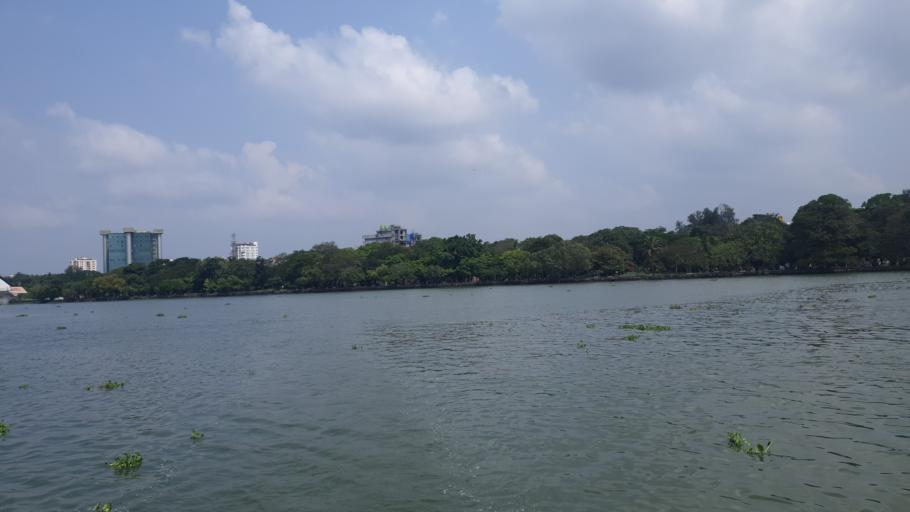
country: IN
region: Kerala
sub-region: Ernakulam
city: Cochin
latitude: 9.9680
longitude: 76.2774
